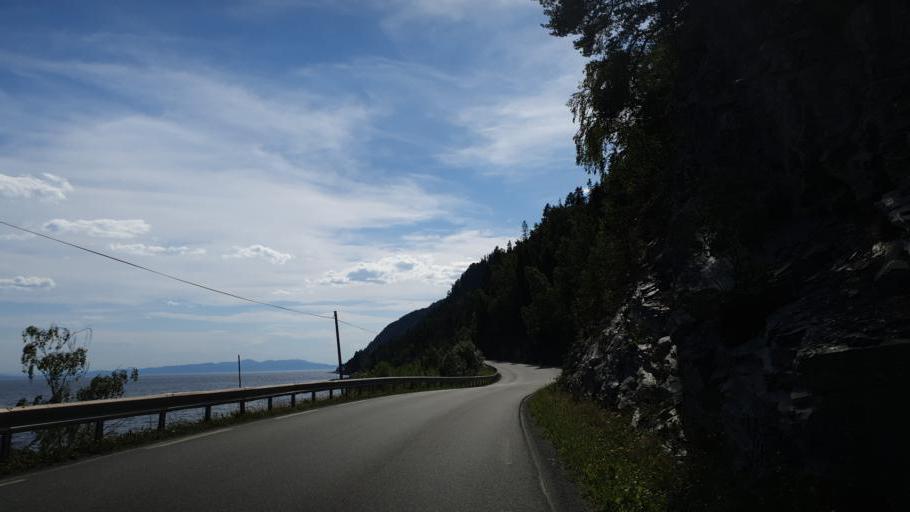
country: NO
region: Nord-Trondelag
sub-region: Leksvik
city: Leksvik
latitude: 63.6443
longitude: 10.5970
